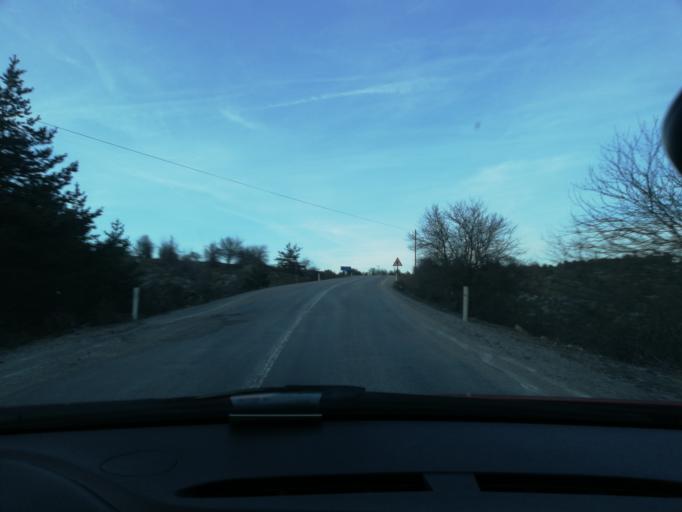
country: TR
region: Kastamonu
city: Agli
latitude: 41.7127
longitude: 33.6536
